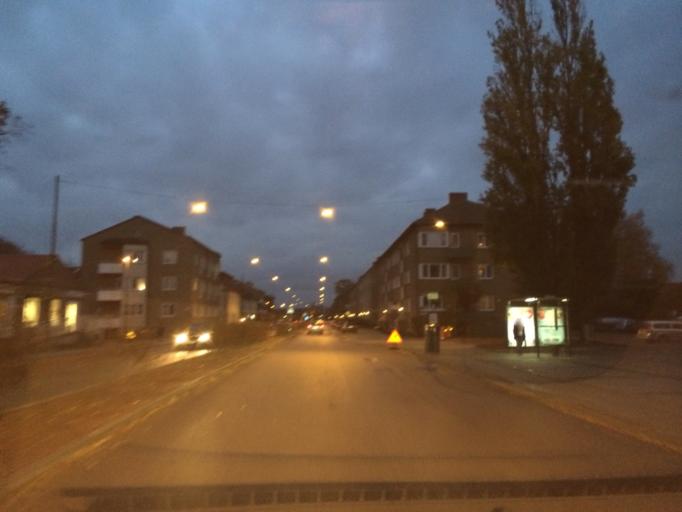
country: SE
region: Skane
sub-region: Malmo
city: Bunkeflostrand
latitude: 55.5813
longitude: 12.9373
